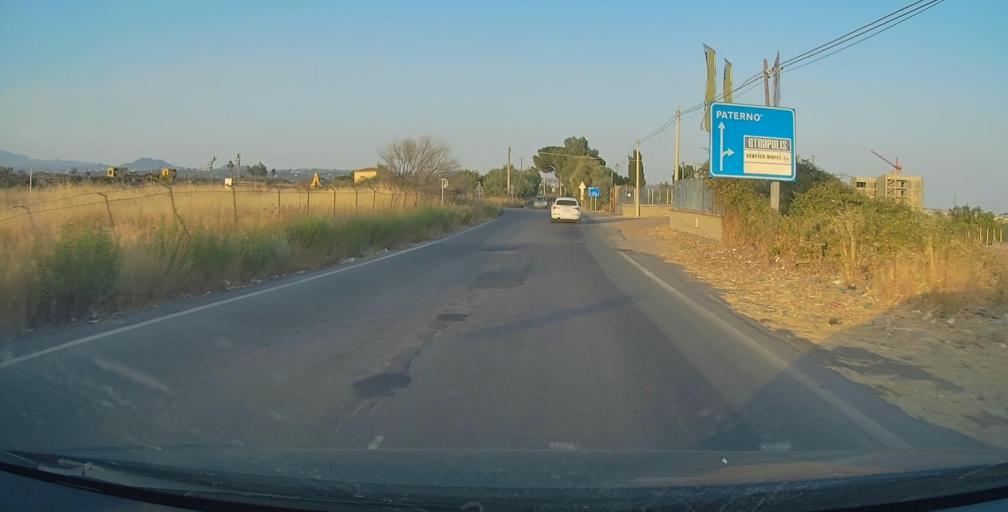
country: IT
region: Sicily
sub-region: Catania
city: Palazzolo
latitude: 37.5495
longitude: 14.9434
